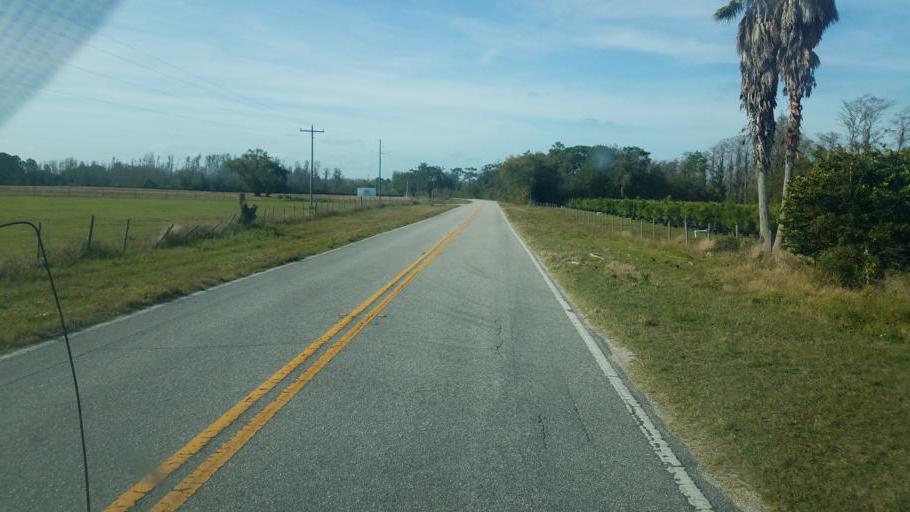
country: US
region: Florida
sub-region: Lake County
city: Clermont
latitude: 28.4356
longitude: -81.8050
